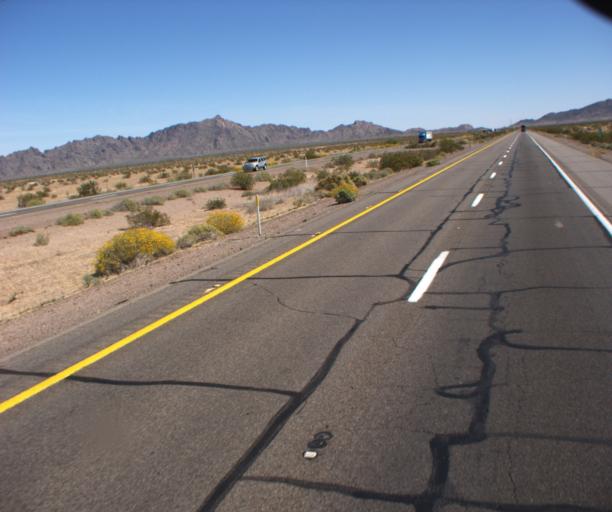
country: US
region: Arizona
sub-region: Yuma County
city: Wellton
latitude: 32.7136
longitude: -113.8199
